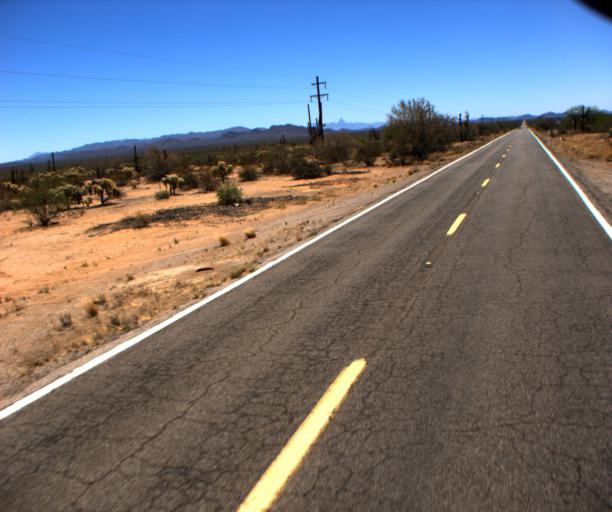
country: US
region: Arizona
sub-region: Pima County
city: Sells
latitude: 32.1024
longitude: -112.0674
